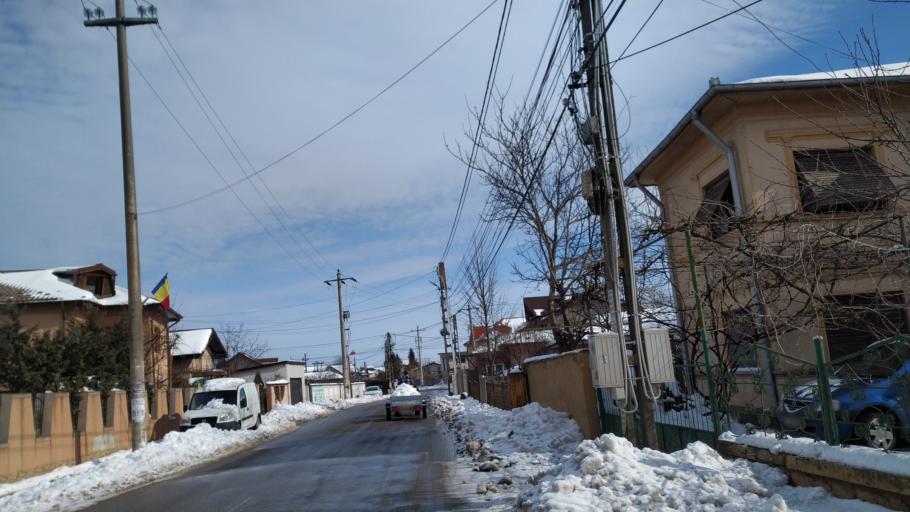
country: RO
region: Ilfov
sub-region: Comuna Berceni
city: Berceni
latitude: 44.3173
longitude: 26.1882
